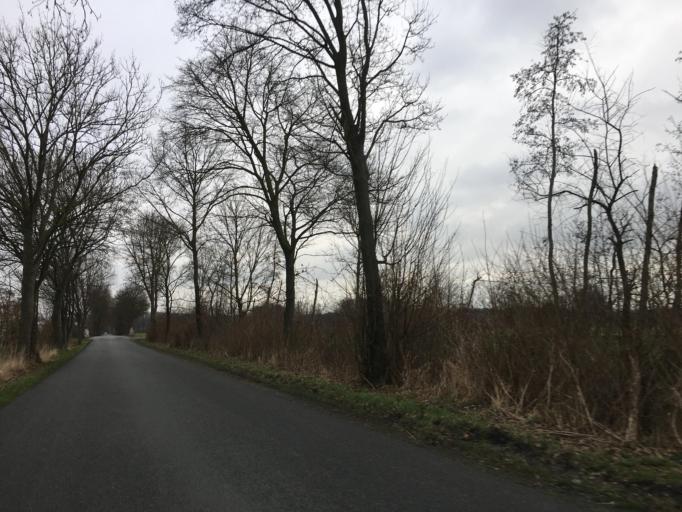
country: DE
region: North Rhine-Westphalia
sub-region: Regierungsbezirk Munster
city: Senden
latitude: 51.8779
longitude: 7.4609
